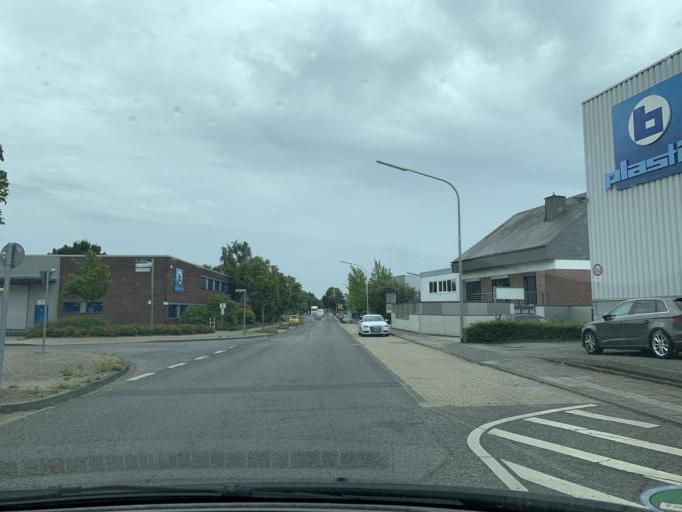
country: DE
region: North Rhine-Westphalia
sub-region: Regierungsbezirk Dusseldorf
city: Monchengladbach
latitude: 51.1416
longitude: 6.4127
